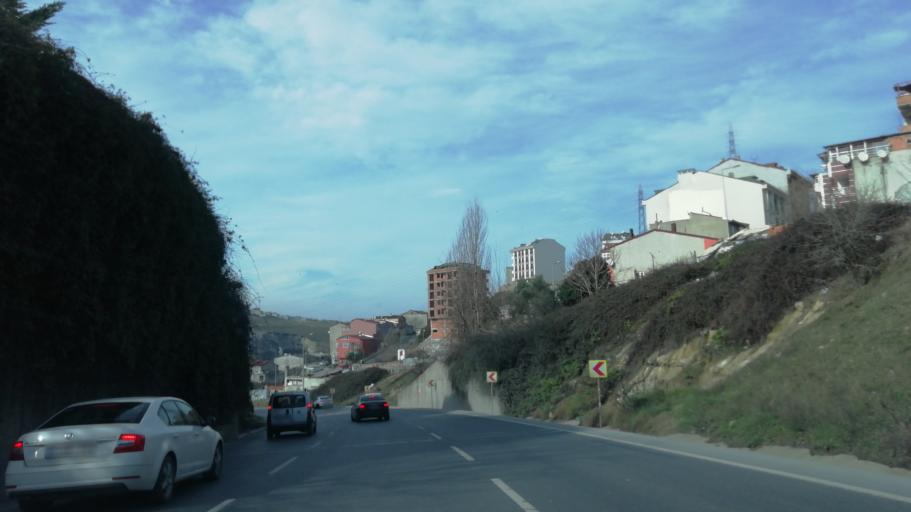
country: TR
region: Istanbul
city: Basaksehir
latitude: 41.0639
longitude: 28.7508
